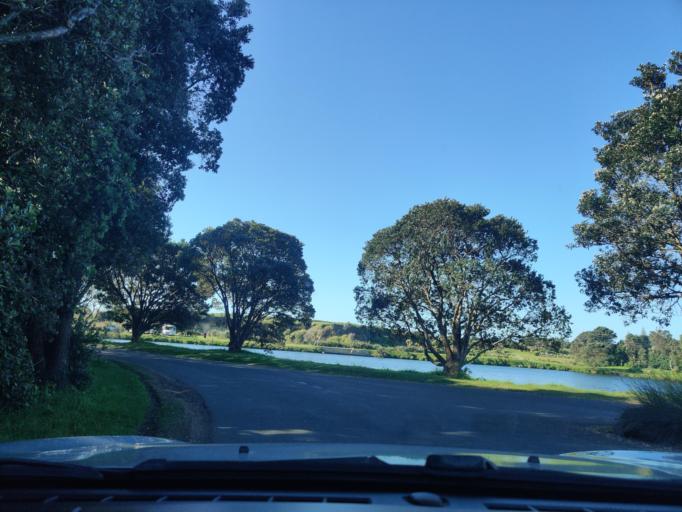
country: NZ
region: Taranaki
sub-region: New Plymouth District
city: New Plymouth
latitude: -39.0396
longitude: 174.1139
